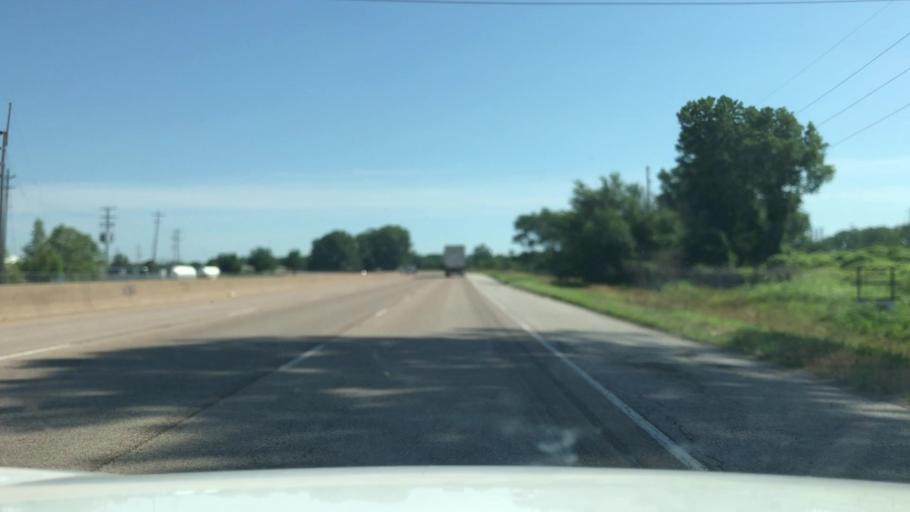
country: US
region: Illinois
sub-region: Madison County
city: Madison
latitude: 38.6912
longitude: -90.1691
